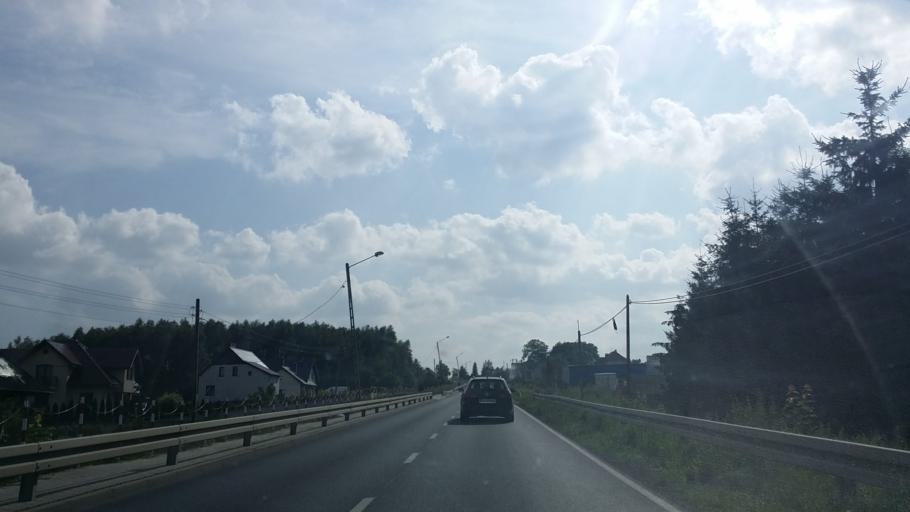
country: PL
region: West Pomeranian Voivodeship
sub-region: Powiat mysliborski
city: Barlinek
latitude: 52.9843
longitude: 15.1994
